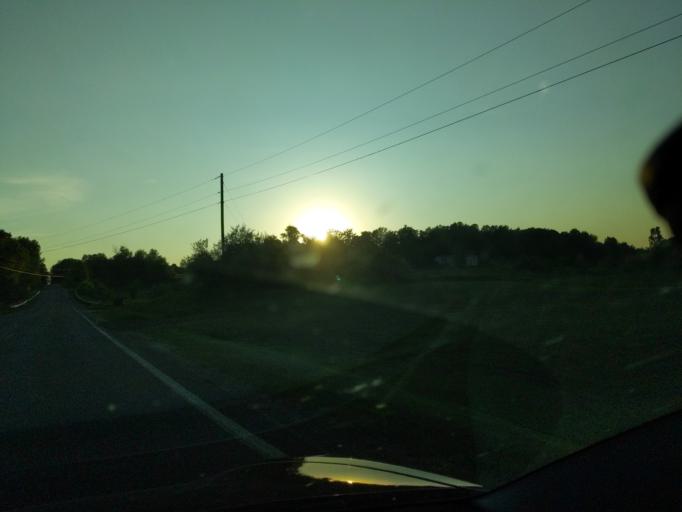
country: US
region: Michigan
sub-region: Barry County
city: Nashville
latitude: 42.5380
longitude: -85.1103
